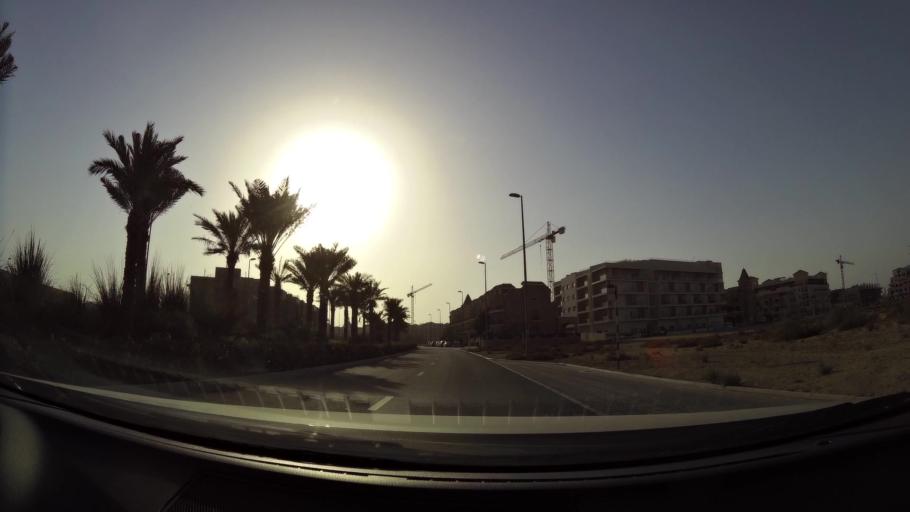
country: AE
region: Dubai
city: Dubai
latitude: 25.0627
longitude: 55.2124
